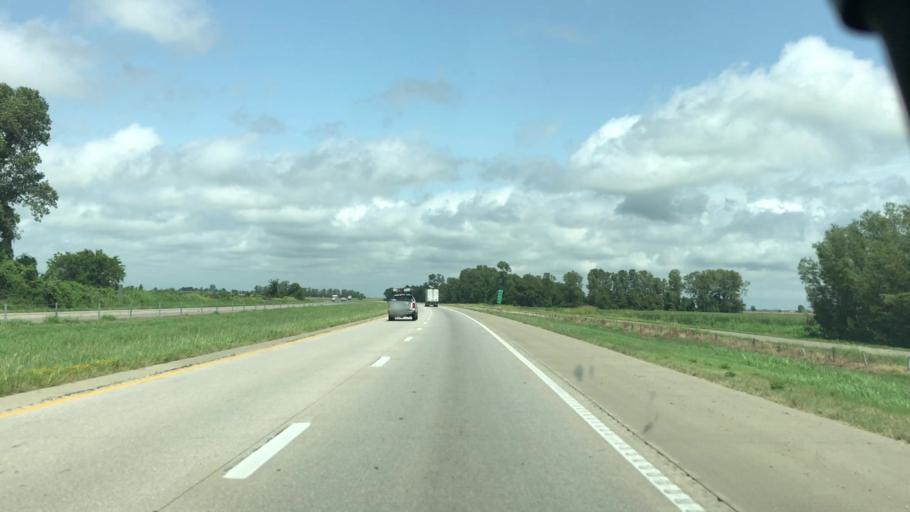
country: US
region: Missouri
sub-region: Pemiscot County
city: Steele
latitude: 36.1234
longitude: -89.7569
